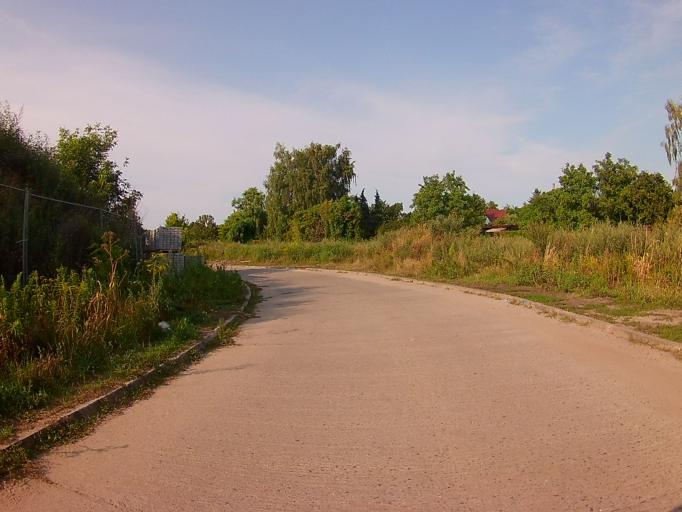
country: DE
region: Berlin
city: Kaulsdorf
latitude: 52.5016
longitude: 13.5771
